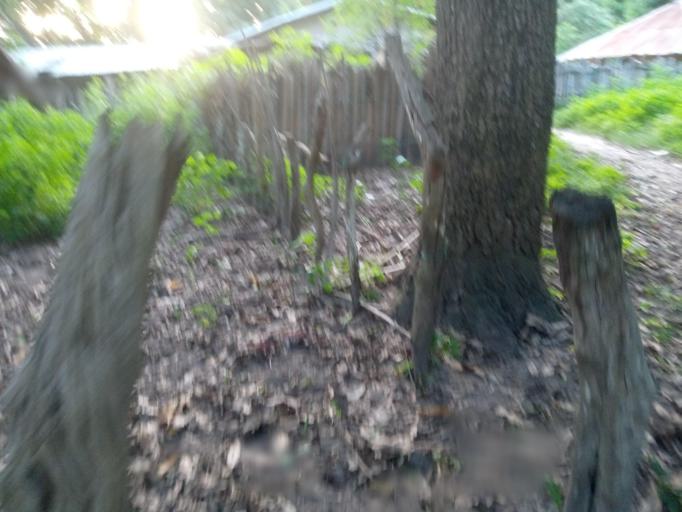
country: GM
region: Western
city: Gunjur
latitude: 13.0430
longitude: -16.7287
